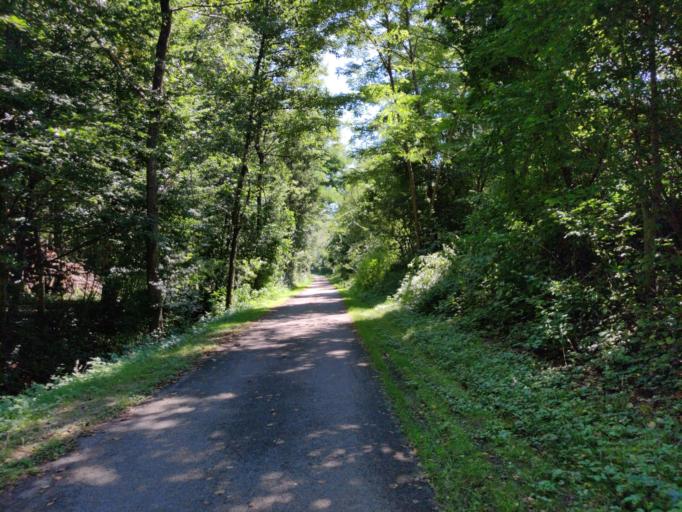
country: AT
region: Styria
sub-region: Politischer Bezirk Leibnitz
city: Ehrenhausen
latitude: 46.7274
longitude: 15.5932
